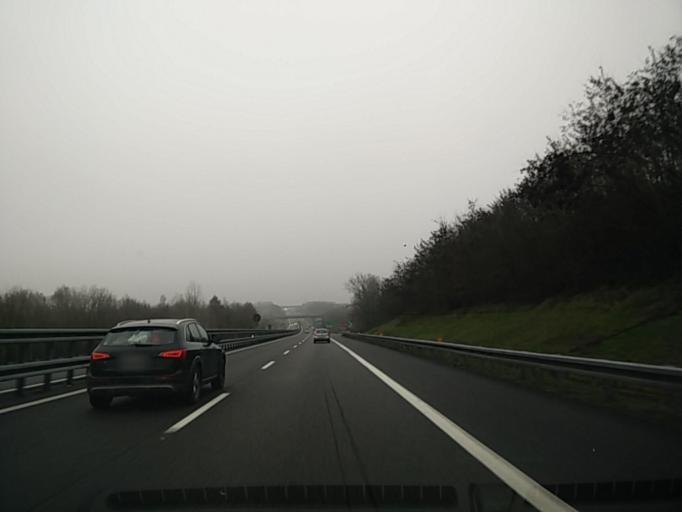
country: IT
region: Piedmont
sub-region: Provincia di Alessandria
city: Quattordio
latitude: 44.9067
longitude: 8.3926
